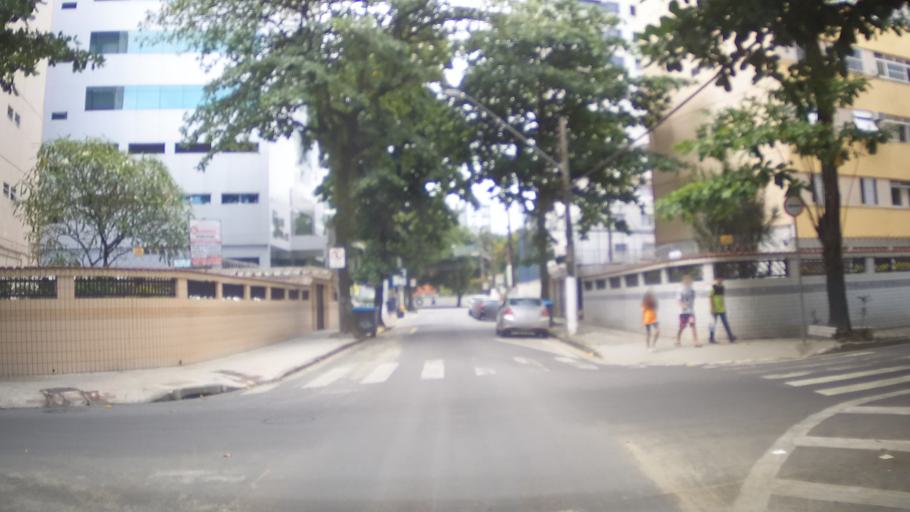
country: BR
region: Sao Paulo
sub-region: Santos
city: Santos
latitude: -23.9542
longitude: -46.3299
